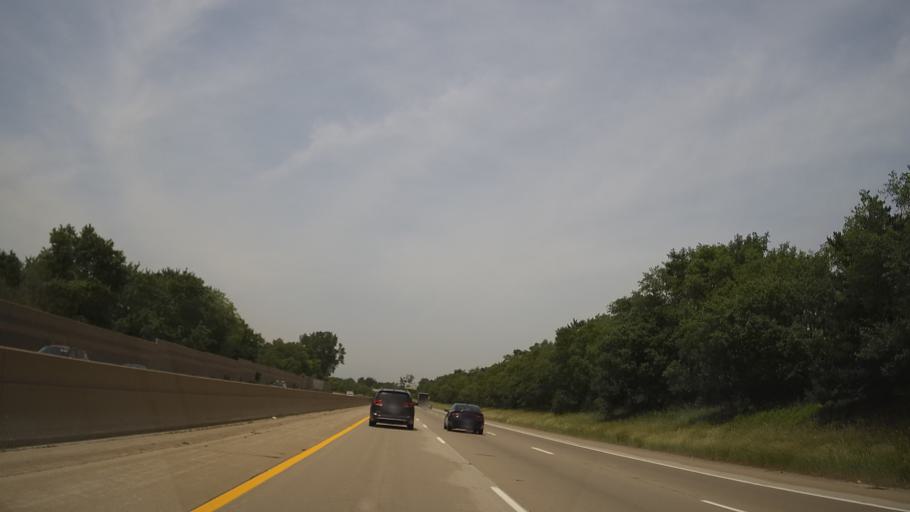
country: US
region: Michigan
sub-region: Washtenaw County
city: Ypsilanti
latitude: 42.2271
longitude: -83.5717
